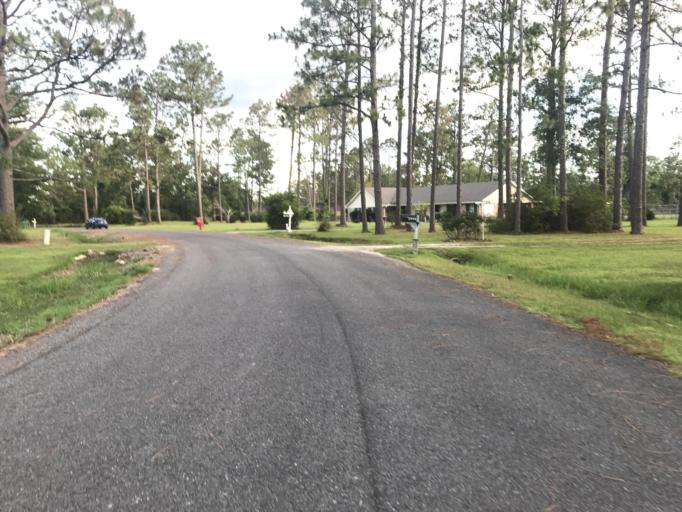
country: US
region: Louisiana
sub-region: Calcasieu Parish
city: Moss Bluff
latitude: 30.3392
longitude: -93.2615
